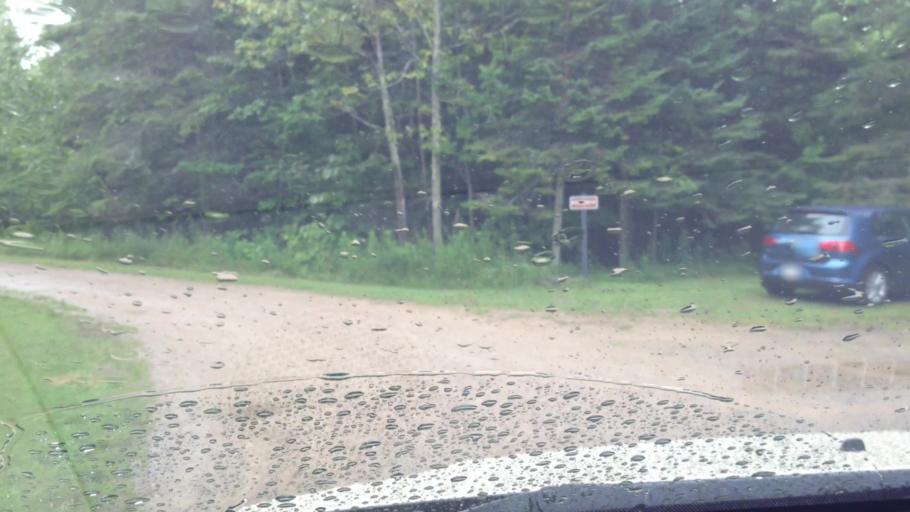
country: US
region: Michigan
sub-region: Menominee County
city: Menominee
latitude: 45.4011
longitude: -87.3603
